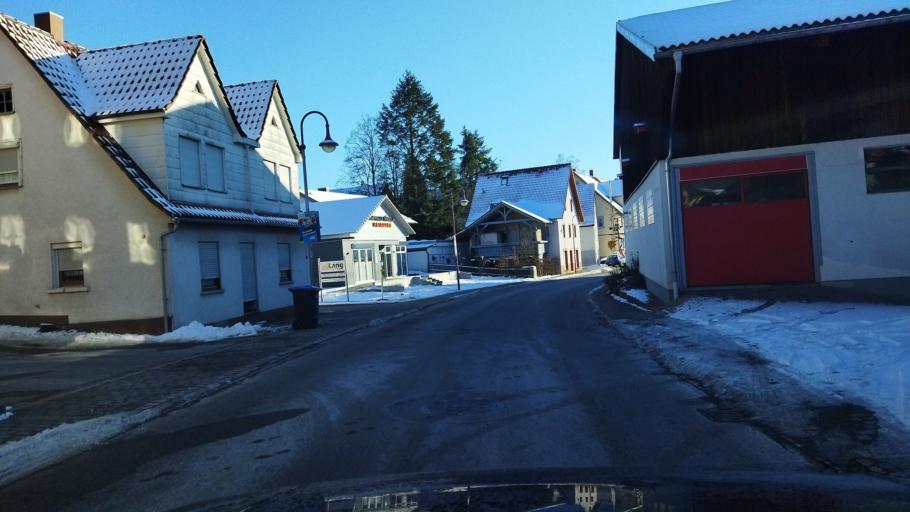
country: DE
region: Baden-Wuerttemberg
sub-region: Regierungsbezirk Stuttgart
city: Buhlerzell
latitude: 49.0044
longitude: 9.9193
